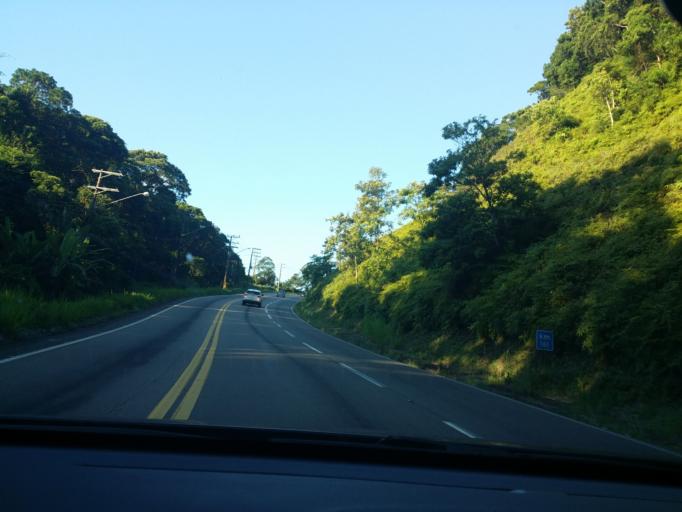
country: BR
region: Sao Paulo
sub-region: Sao Sebastiao
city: Sao Sebastiao
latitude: -23.7827
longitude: -45.6098
